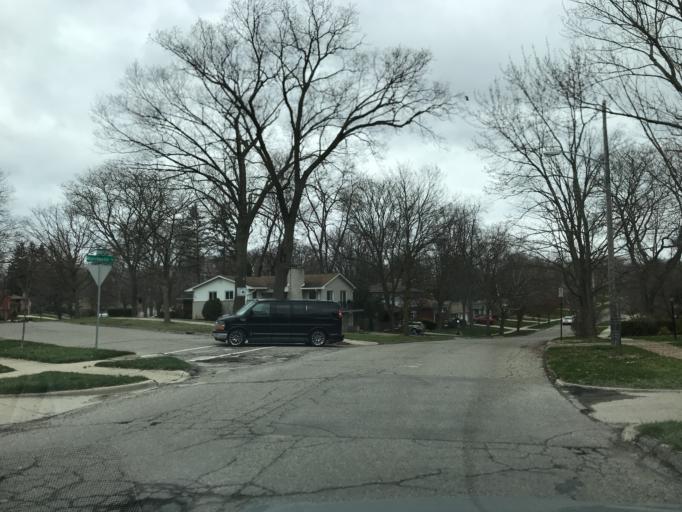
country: US
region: Michigan
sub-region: Washtenaw County
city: Ann Arbor
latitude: 42.2539
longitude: -83.7144
